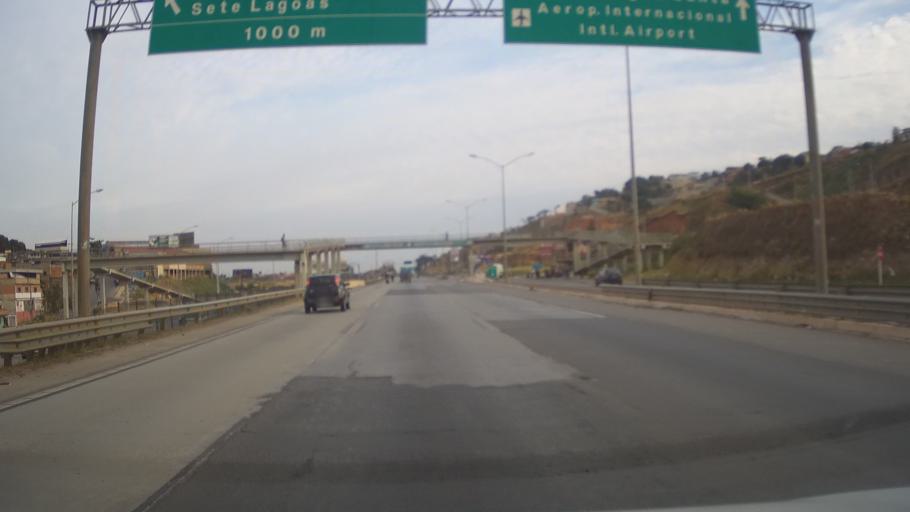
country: BR
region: Minas Gerais
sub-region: Vespasiano
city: Vespasiano
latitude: -19.7731
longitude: -43.9485
